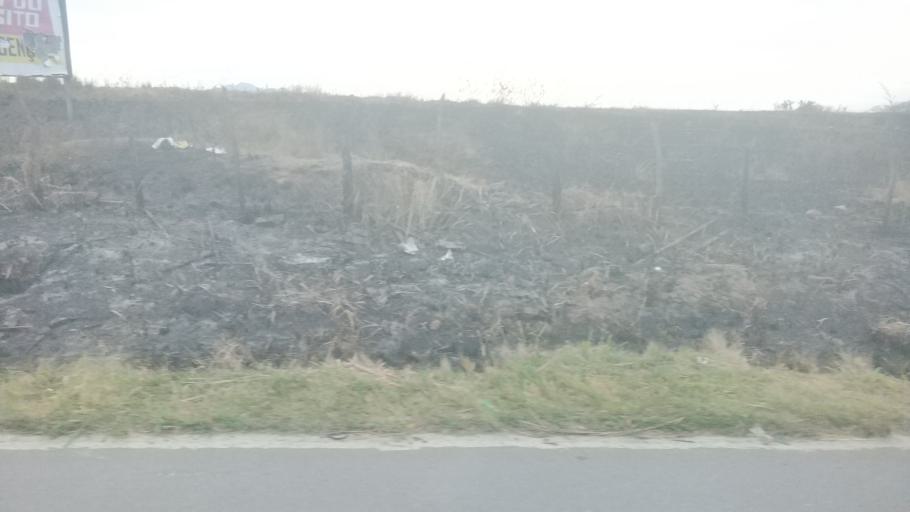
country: BR
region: Rio de Janeiro
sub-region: Seropedica
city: Seropedica
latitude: -22.7846
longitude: -43.6566
